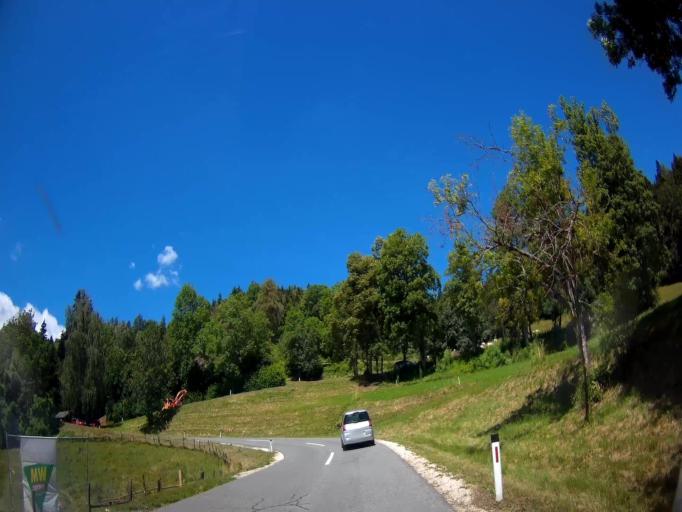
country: AT
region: Carinthia
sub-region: Politischer Bezirk Sankt Veit an der Glan
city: St. Georgen am Laengsee
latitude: 46.7235
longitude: 14.4319
